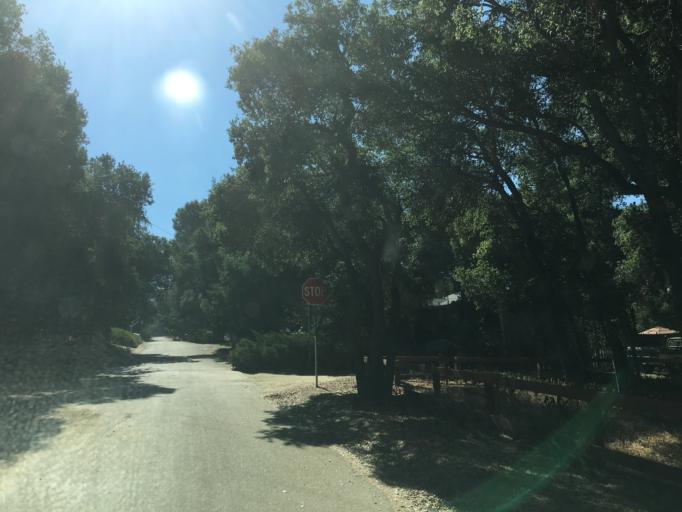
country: US
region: California
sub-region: Los Angeles County
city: Green Valley
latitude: 34.6182
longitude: -118.4095
